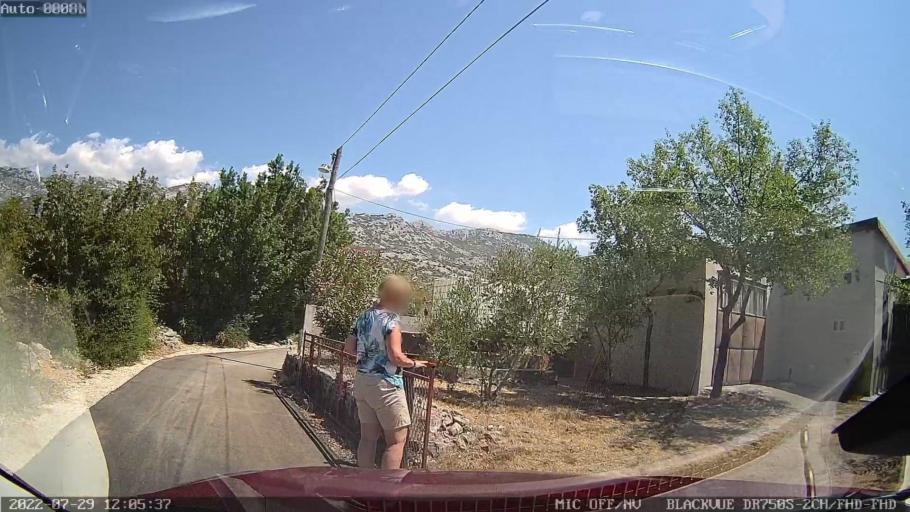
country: HR
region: Zadarska
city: Starigrad
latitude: 44.2741
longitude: 15.4957
